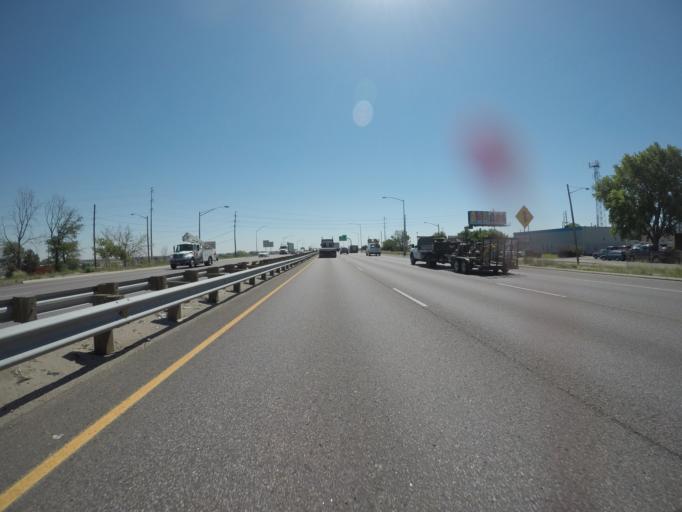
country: US
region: Colorado
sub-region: Adams County
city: Commerce City
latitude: 39.7783
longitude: -104.9098
